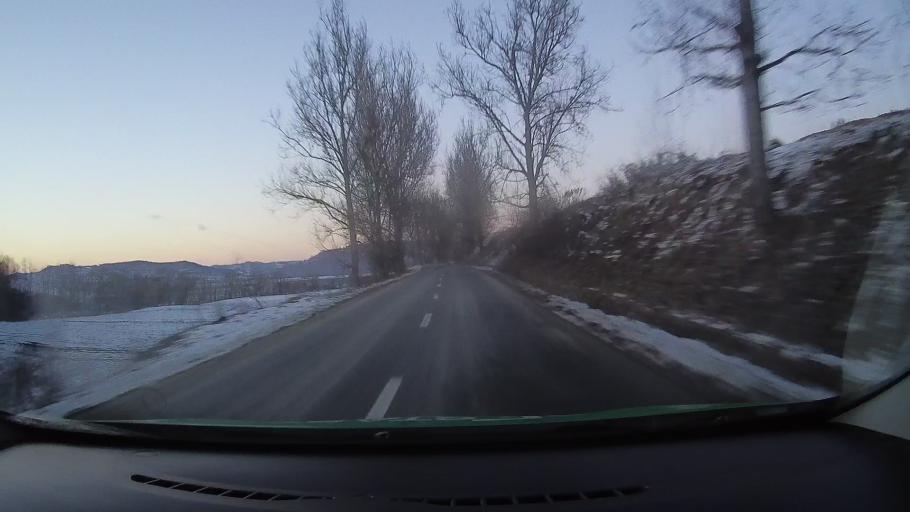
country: RO
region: Sibiu
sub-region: Comuna Alma
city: Alma
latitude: 46.1861
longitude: 24.4712
